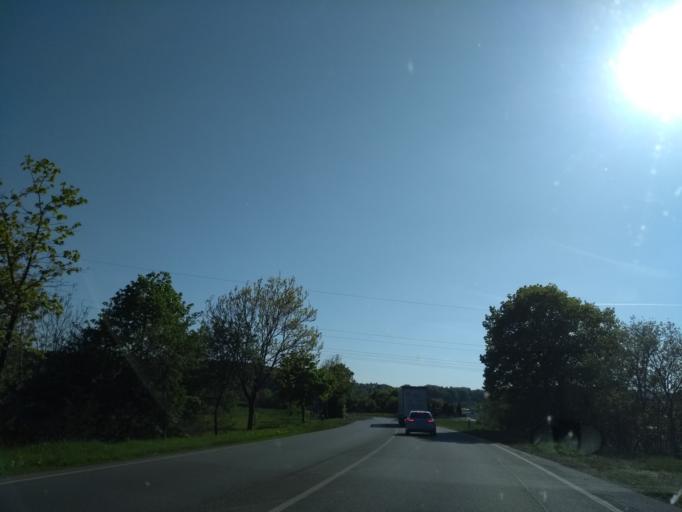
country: DE
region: Hesse
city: Allendorf
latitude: 51.0209
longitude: 8.6697
